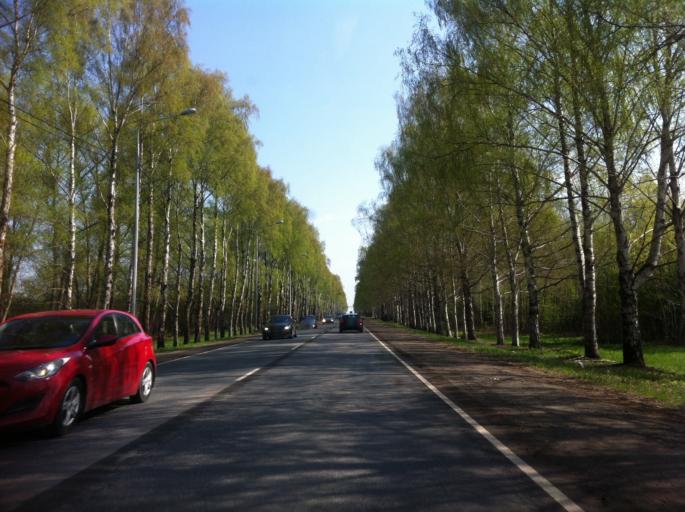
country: RU
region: Pskov
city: Pskov
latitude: 57.7989
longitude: 28.2359
